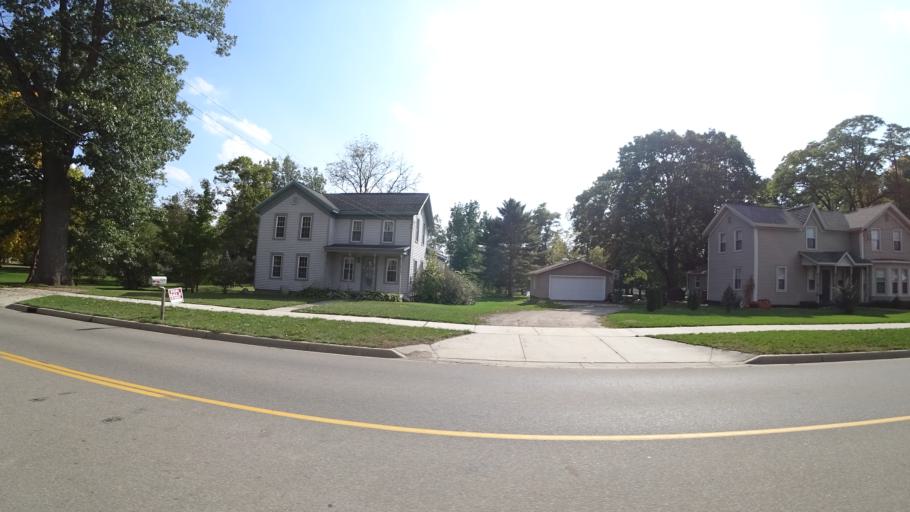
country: US
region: Michigan
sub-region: Saint Joseph County
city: Centreville
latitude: 42.0066
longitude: -85.4459
